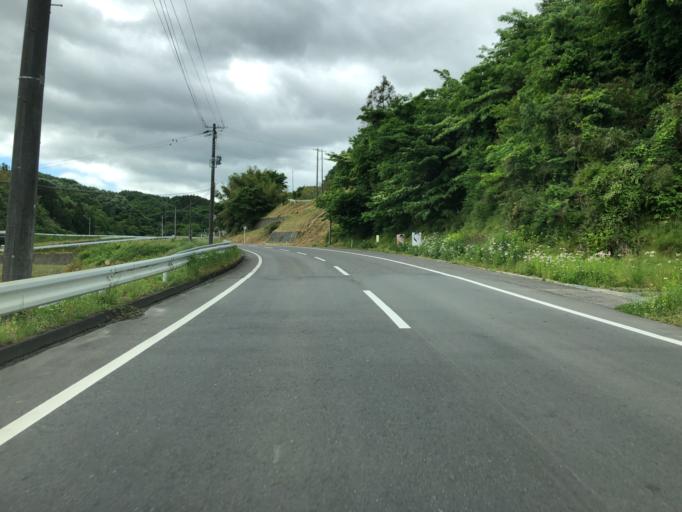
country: JP
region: Fukushima
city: Nihommatsu
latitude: 37.5454
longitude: 140.4601
